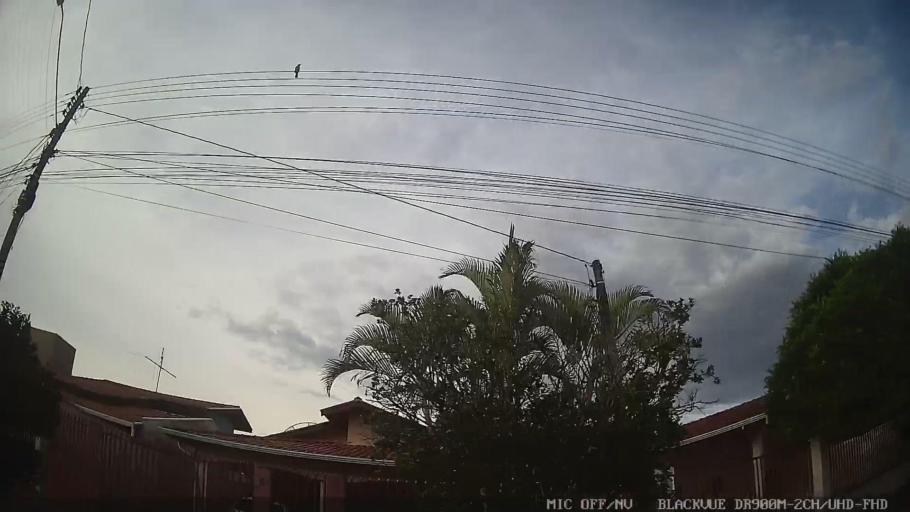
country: BR
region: Sao Paulo
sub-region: Jaguariuna
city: Jaguariuna
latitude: -22.6442
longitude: -47.0487
